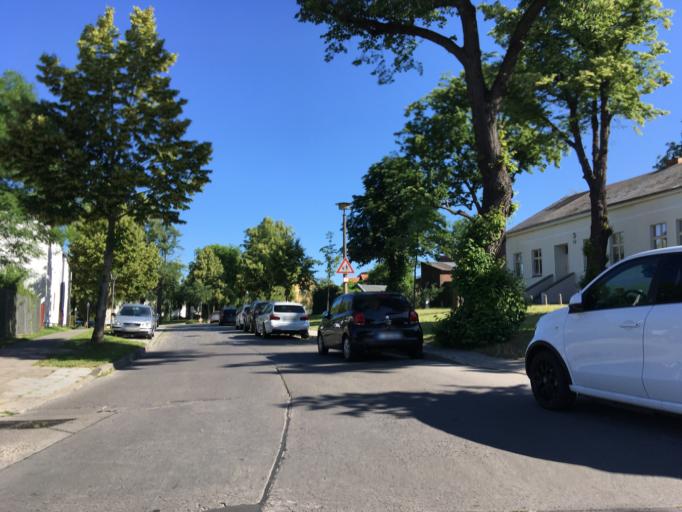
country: DE
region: Berlin
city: Kaulsdorf
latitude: 52.5065
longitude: 13.5821
